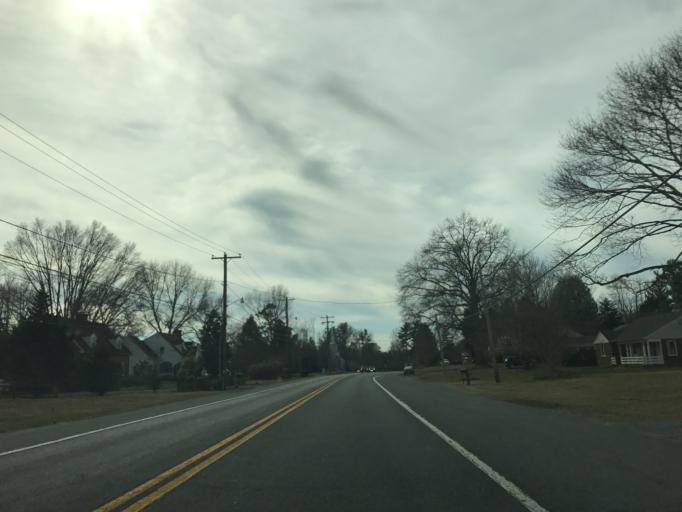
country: US
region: Maryland
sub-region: Queen Anne's County
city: Centreville
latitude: 39.0510
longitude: -76.0567
